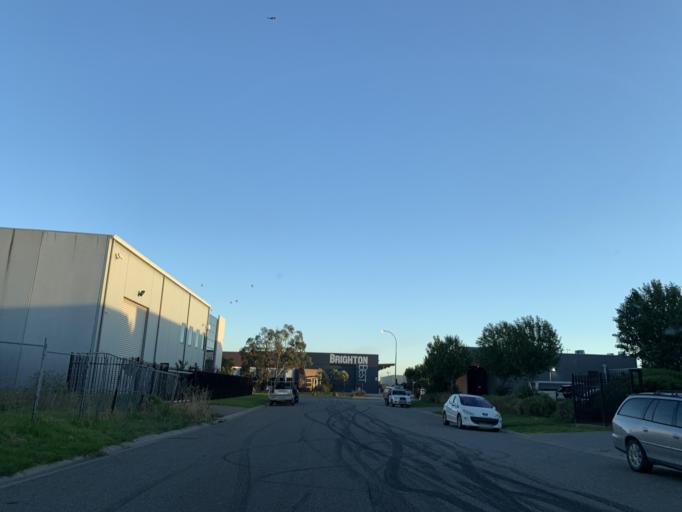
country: AU
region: Victoria
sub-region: Kingston
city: Aspendale Gardens
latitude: -38.0109
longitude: 145.1081
